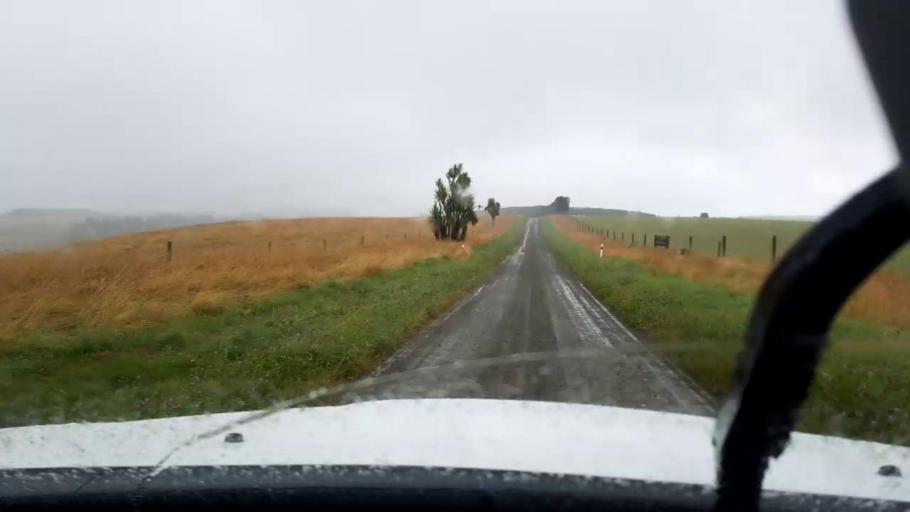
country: NZ
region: Canterbury
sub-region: Timaru District
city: Pleasant Point
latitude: -44.1692
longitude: 171.1599
